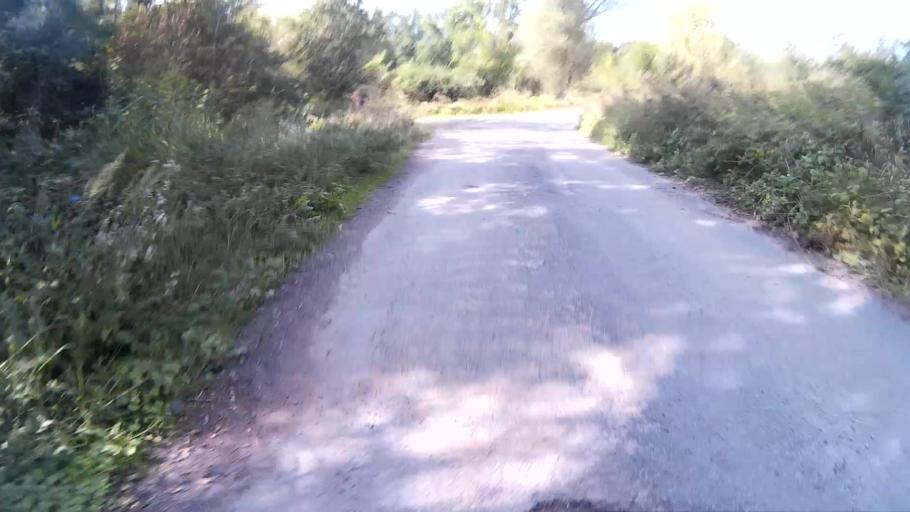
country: CZ
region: South Moravian
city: Hrusovany nad Jevisovkou
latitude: 48.7900
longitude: 16.4323
